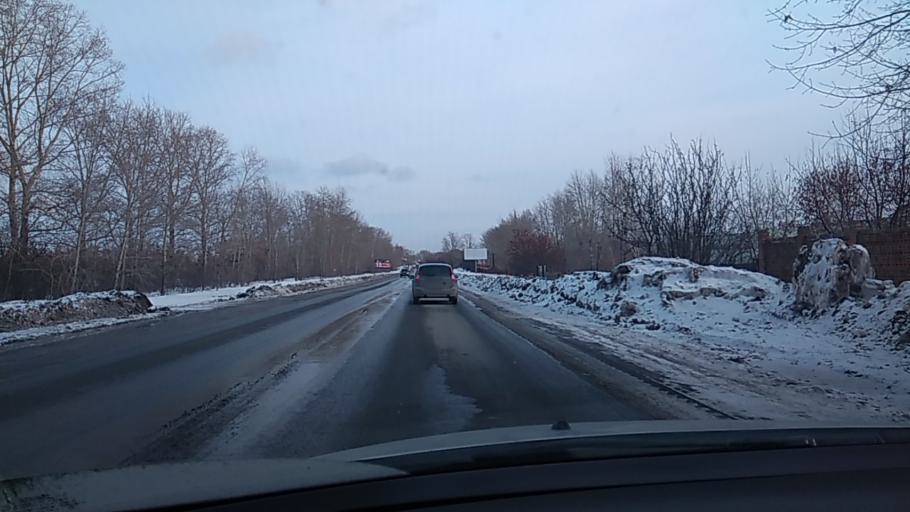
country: RU
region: Sverdlovsk
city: Martyush
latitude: 56.4509
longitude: 61.8003
